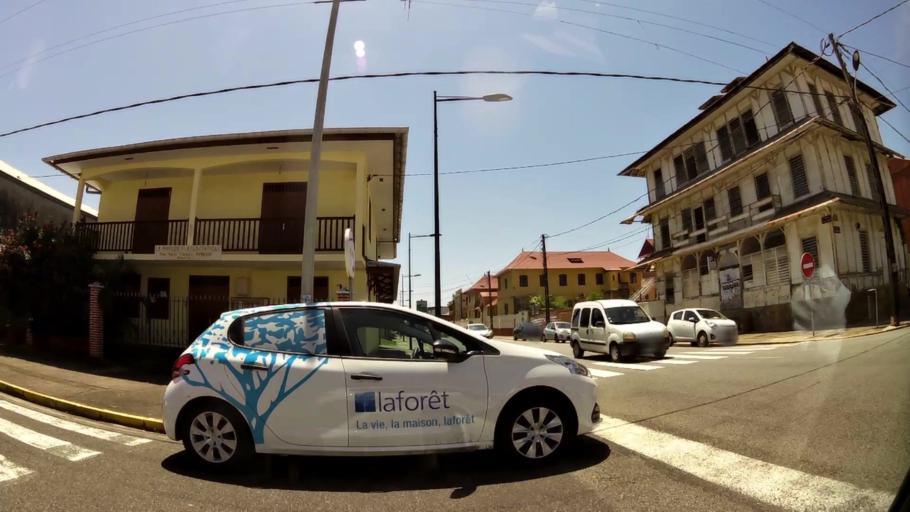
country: GF
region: Guyane
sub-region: Guyane
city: Cayenne
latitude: 4.9414
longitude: -52.3324
